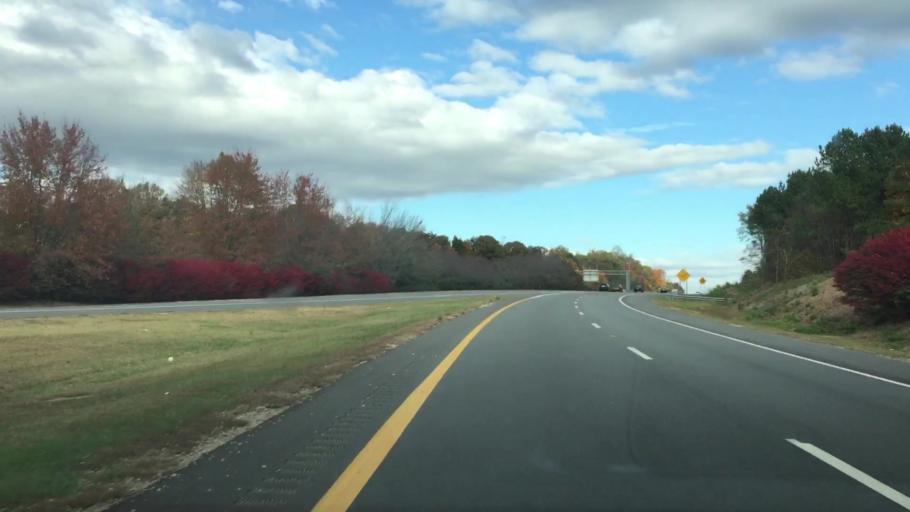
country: US
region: North Carolina
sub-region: Forsyth County
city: Clemmons
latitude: 36.0726
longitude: -80.3246
